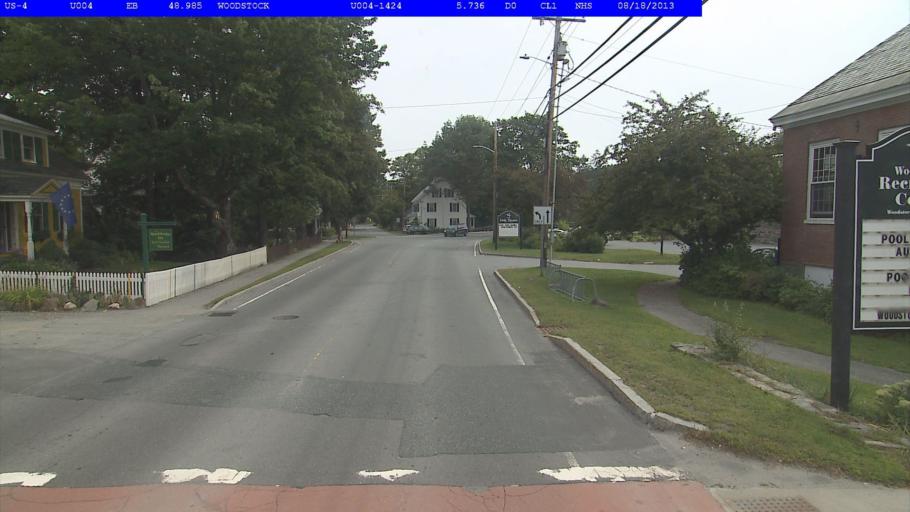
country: US
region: Vermont
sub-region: Windsor County
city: Woodstock
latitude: 43.6220
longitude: -72.5270
